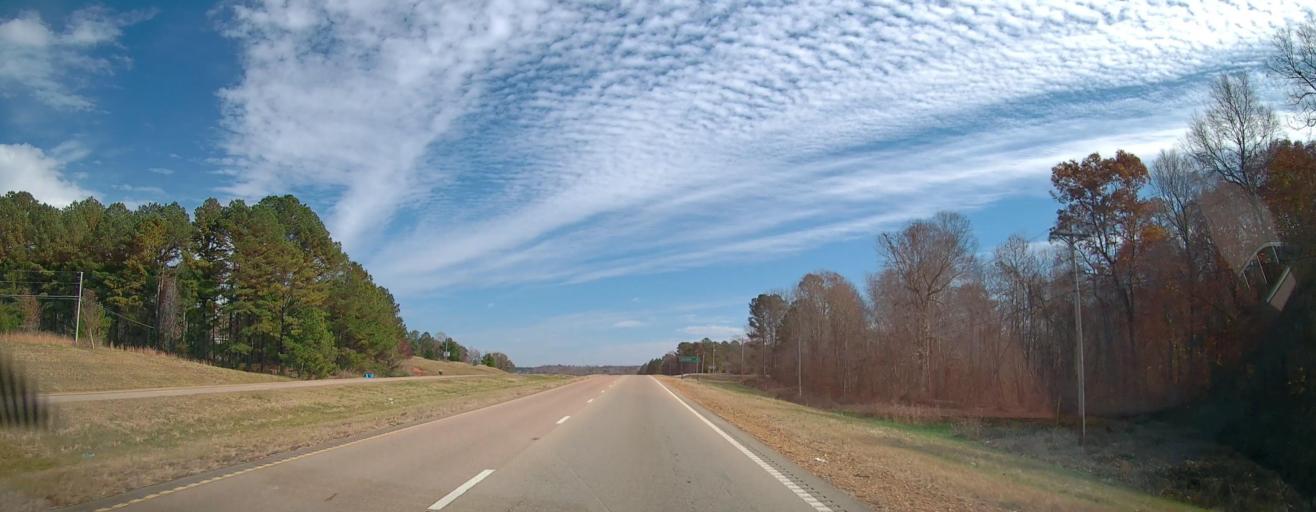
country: US
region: Mississippi
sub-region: Tippah County
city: Ripley
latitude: 34.9520
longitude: -88.8922
